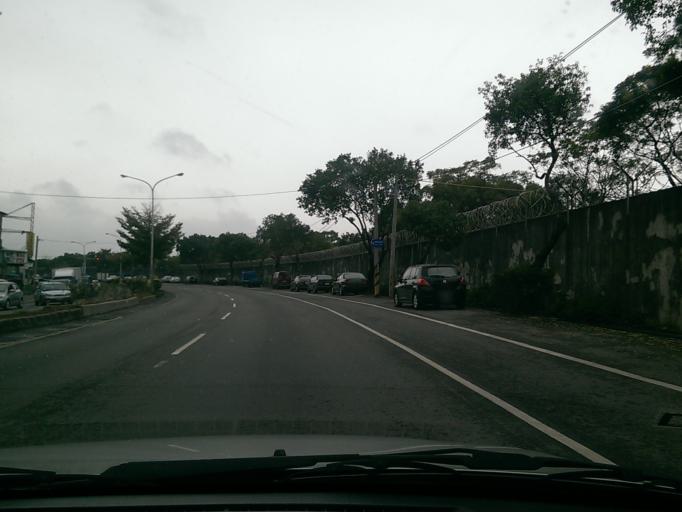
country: TW
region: Taiwan
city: Fengyuan
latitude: 24.2416
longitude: 120.6297
